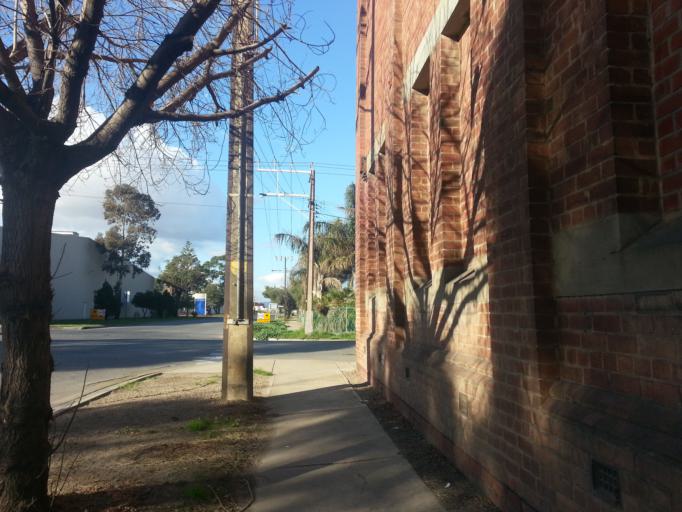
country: AU
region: South Australia
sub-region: Port Adelaide Enfield
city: Alberton
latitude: -34.8460
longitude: 138.5163
